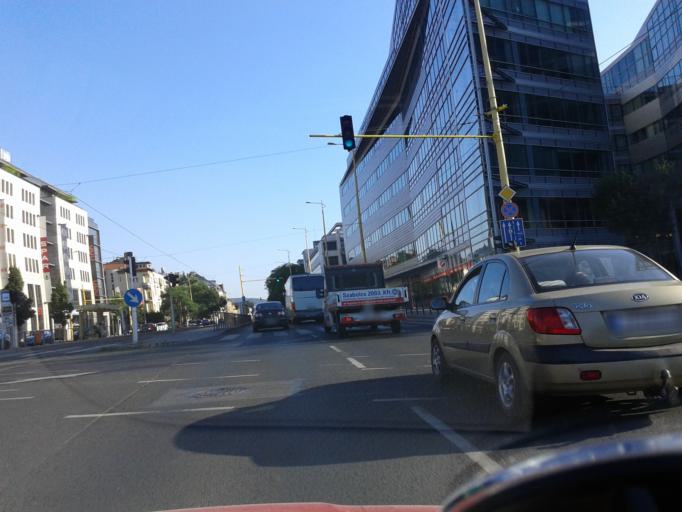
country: HU
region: Budapest
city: Budapest XII. keruelet
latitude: 47.4900
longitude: 19.0248
